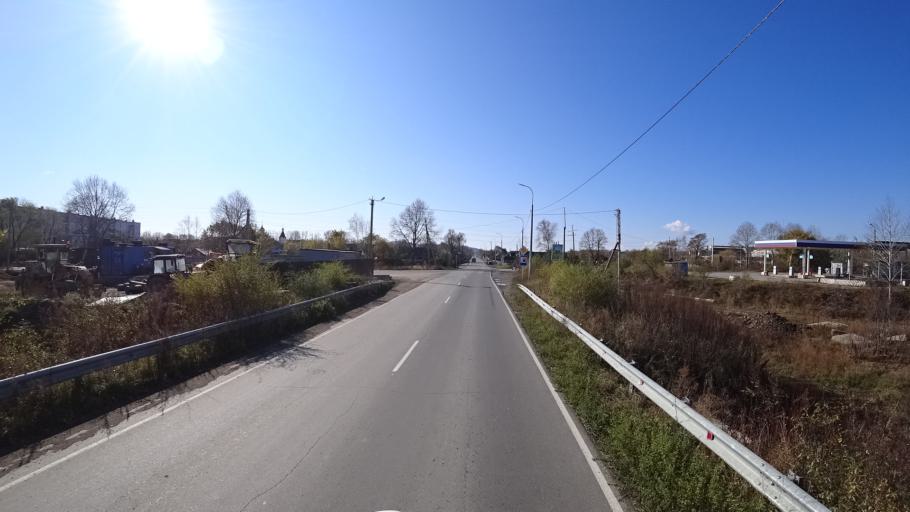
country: RU
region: Khabarovsk Krai
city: Amursk
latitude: 50.1059
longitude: 136.5135
